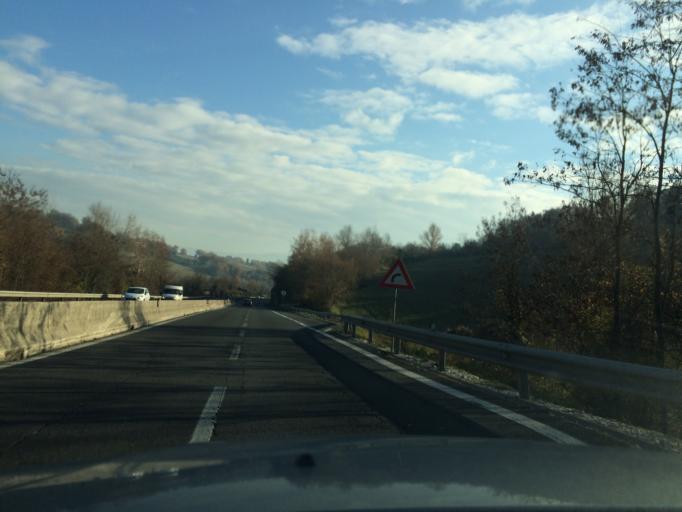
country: IT
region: Umbria
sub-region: Provincia di Terni
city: San Gemini
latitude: 42.6053
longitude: 12.5591
